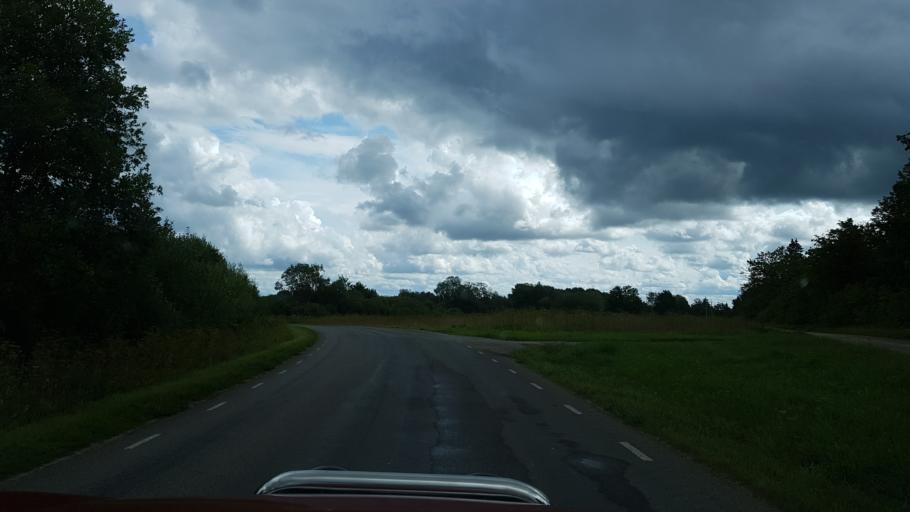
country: EE
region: Laeaene
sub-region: Lihula vald
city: Lihula
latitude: 58.7218
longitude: 23.9594
